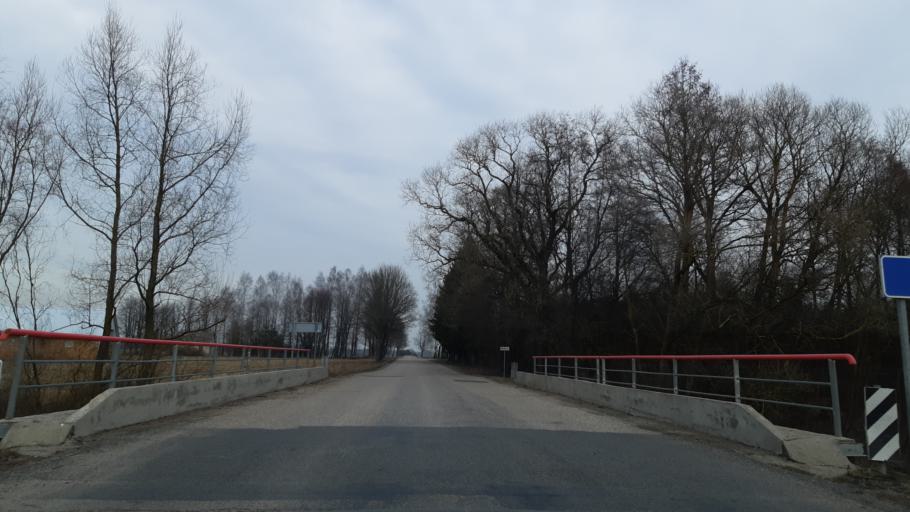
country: LT
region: Marijampoles apskritis
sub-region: Marijampole Municipality
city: Marijampole
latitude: 54.7131
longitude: 23.3181
